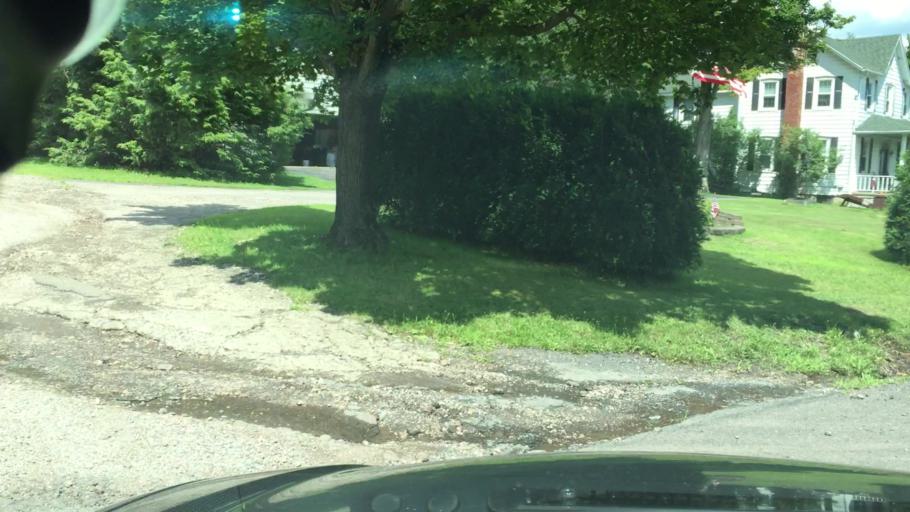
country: US
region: Pennsylvania
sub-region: Luzerne County
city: Freeland
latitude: 41.0315
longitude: -75.9151
